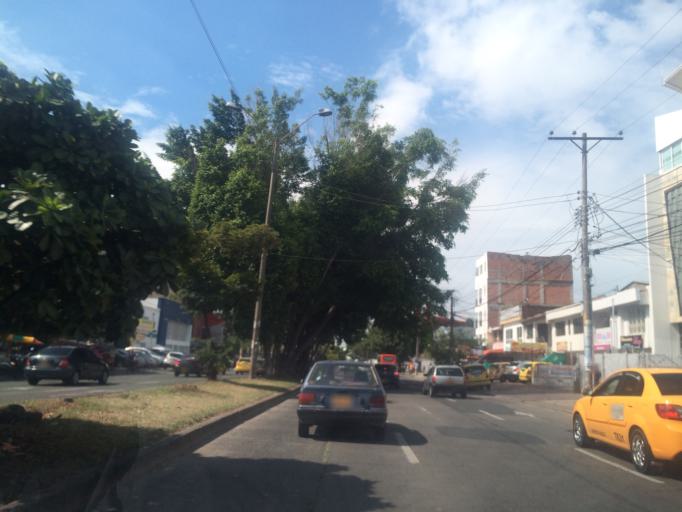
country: CO
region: Valle del Cauca
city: Cali
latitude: 3.4200
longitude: -76.5389
